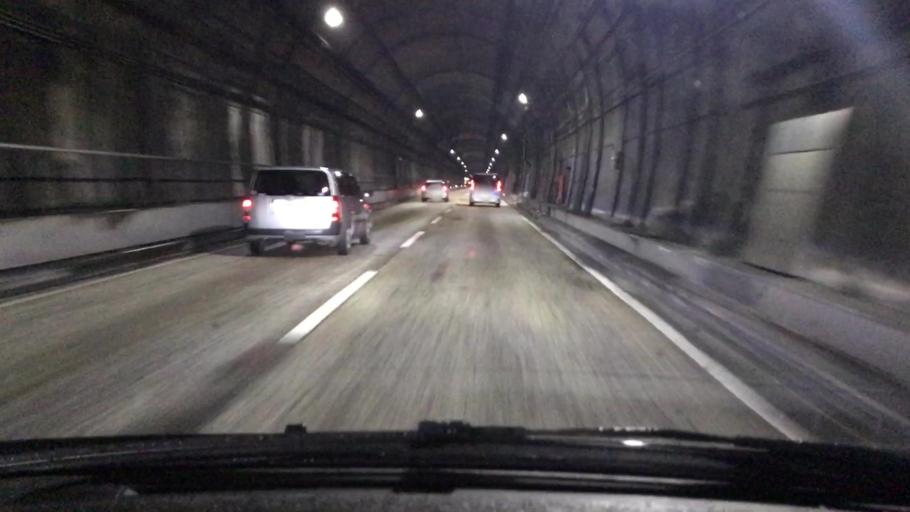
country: JP
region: Hyogo
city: Kobe
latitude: 34.7464
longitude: 135.1687
